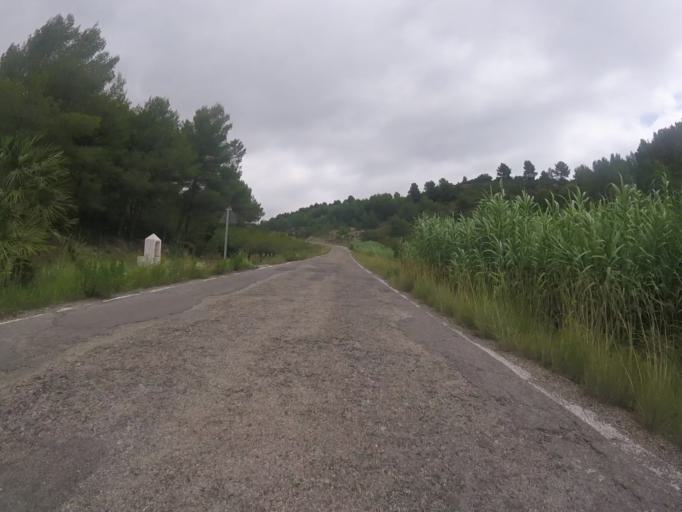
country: ES
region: Valencia
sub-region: Provincia de Castello
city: Cabanes
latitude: 40.1176
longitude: 0.0475
